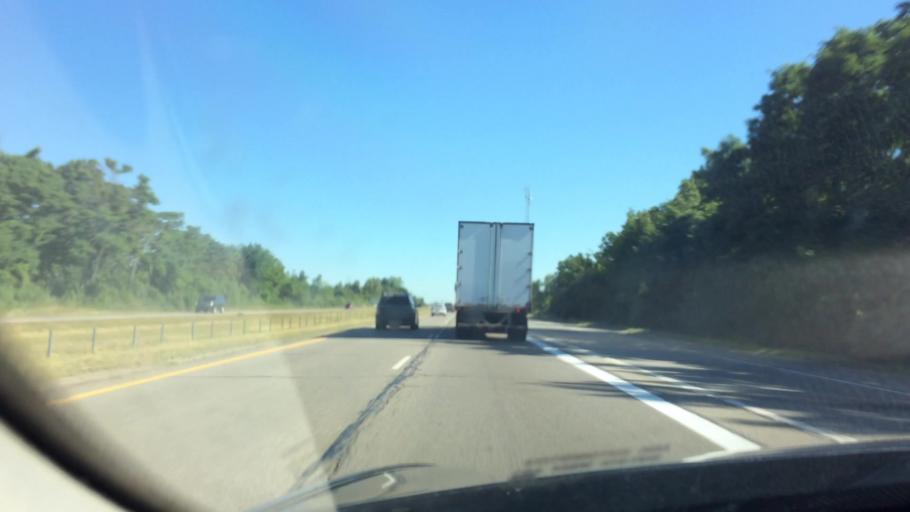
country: US
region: Michigan
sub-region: Washtenaw County
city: Ypsilanti
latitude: 42.2100
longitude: -83.6848
